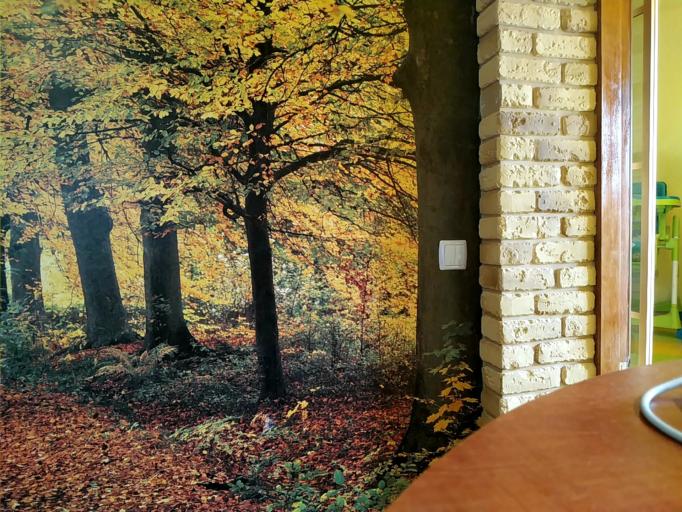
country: RU
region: Tverskaya
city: Kalashnikovo
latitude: 57.3323
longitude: 35.3489
